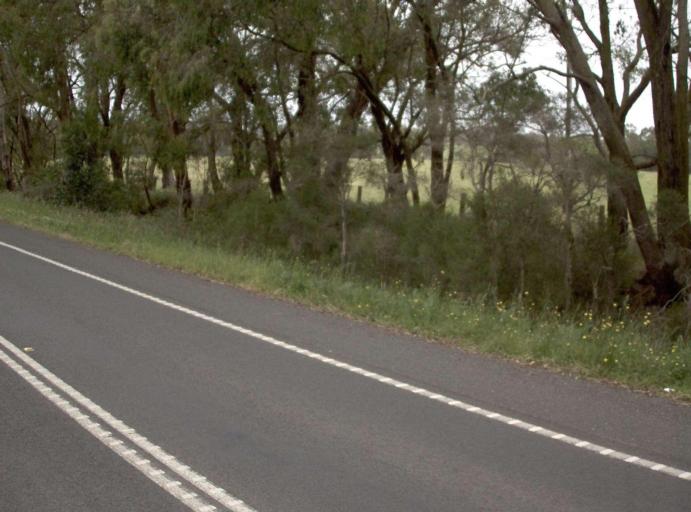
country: AU
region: Victoria
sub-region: Bass Coast
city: North Wonthaggi
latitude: -38.5710
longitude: 145.9757
